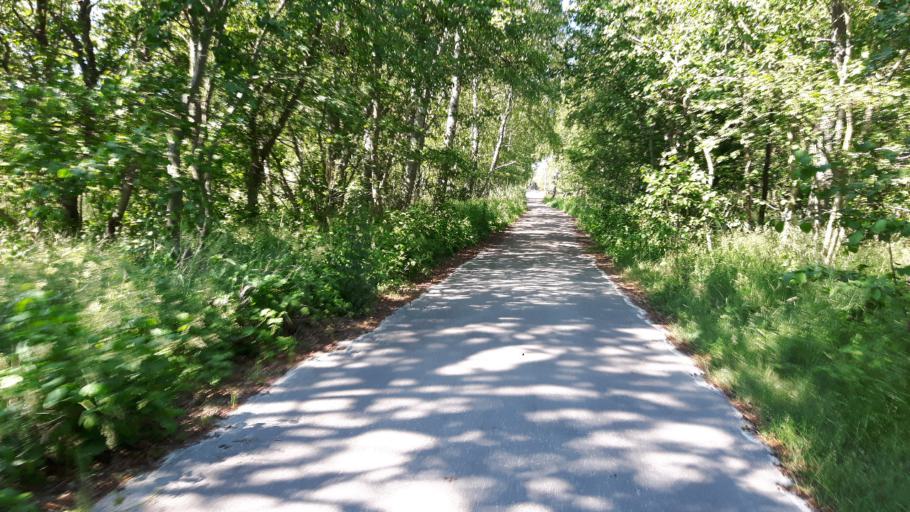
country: LT
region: Klaipedos apskritis
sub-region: Klaipeda
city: Klaipeda
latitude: 55.6884
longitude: 21.1035
